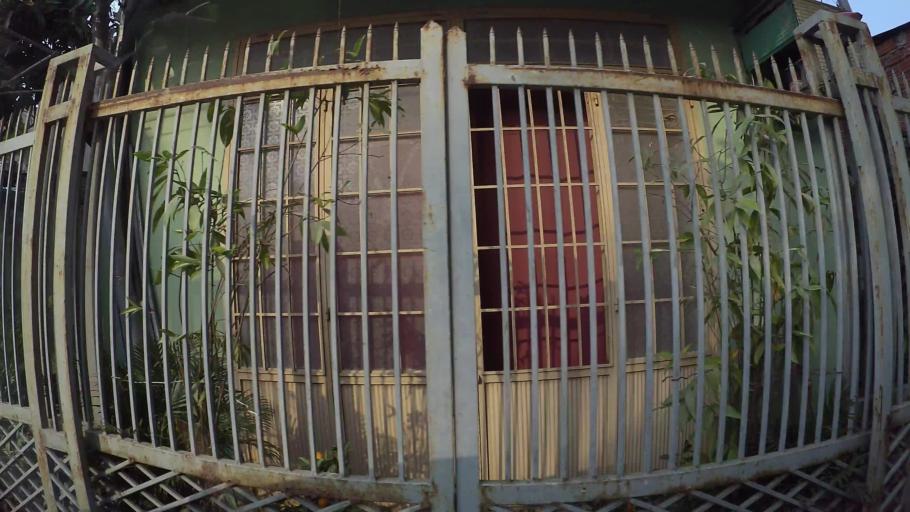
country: VN
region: Da Nang
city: Lien Chieu
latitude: 16.0491
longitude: 108.1520
